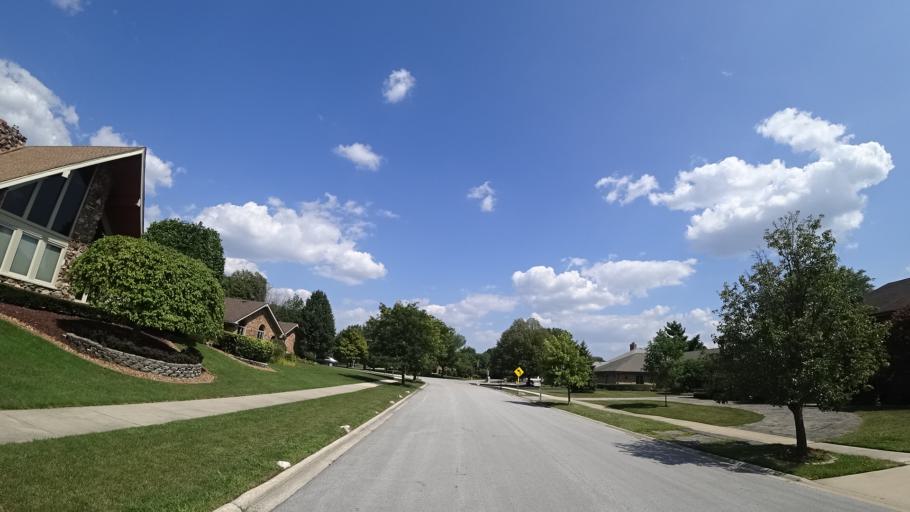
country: US
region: Illinois
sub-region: Cook County
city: Orland Park
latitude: 41.6261
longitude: -87.8260
